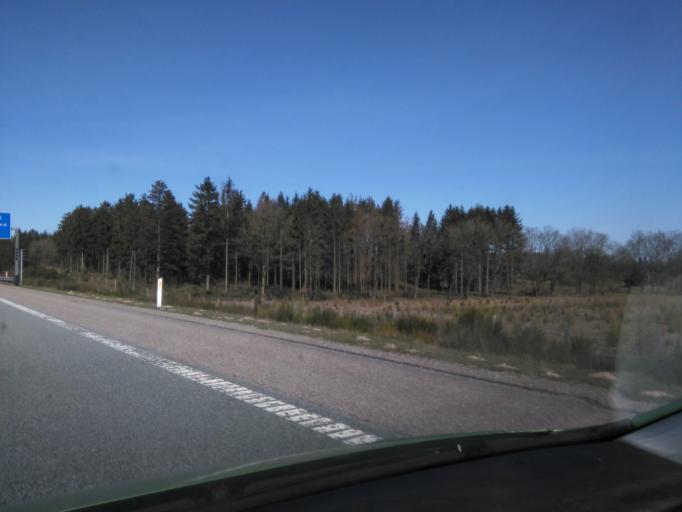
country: DK
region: South Denmark
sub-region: Vejle Kommune
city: Give
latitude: 55.8360
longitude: 9.2997
